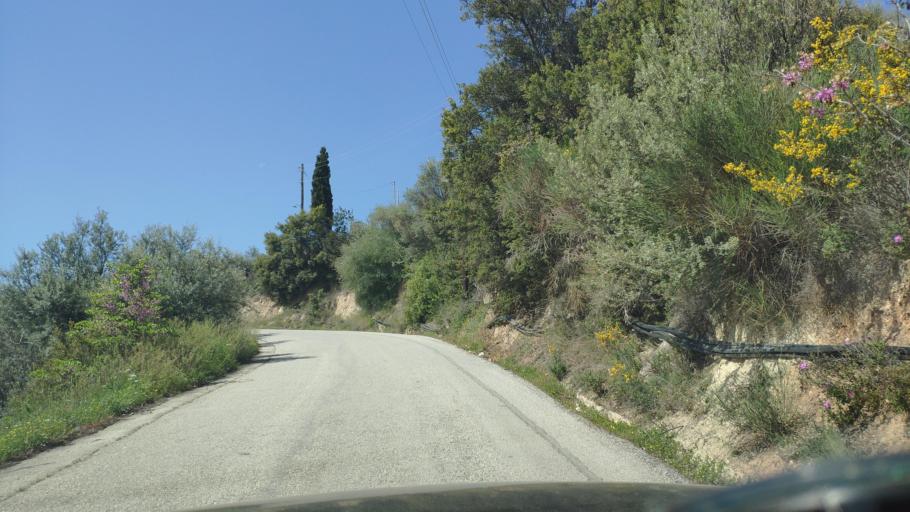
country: GR
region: West Greece
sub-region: Nomos Achaias
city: Aiyira
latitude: 38.1250
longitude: 22.3447
